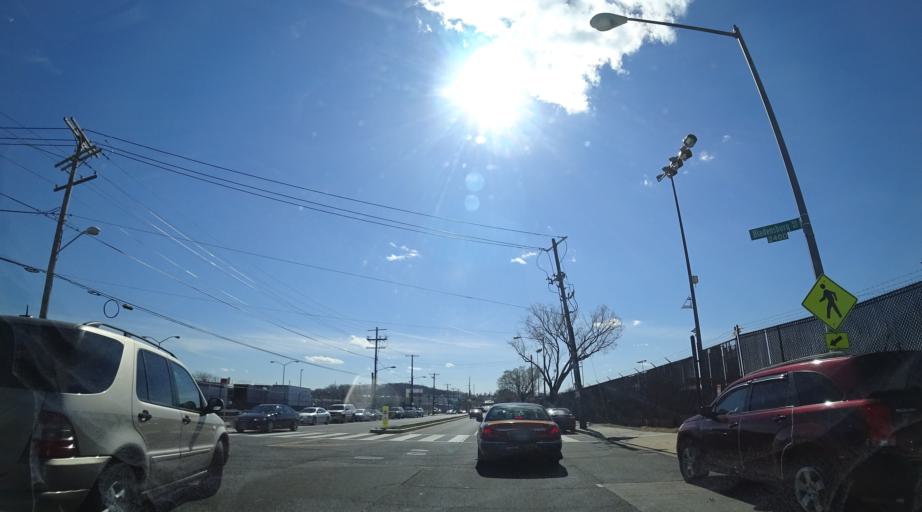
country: US
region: Maryland
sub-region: Prince George's County
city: Mount Rainier
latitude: 38.9227
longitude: -76.9682
